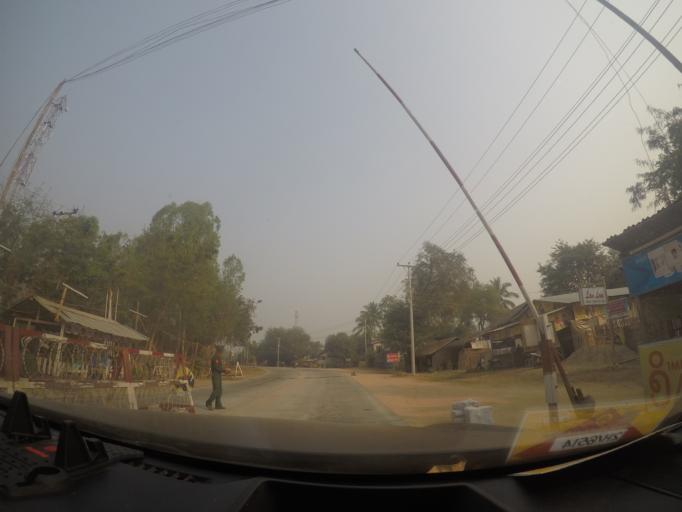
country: MM
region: Mandalay
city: Nay Pyi Taw
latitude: 19.9032
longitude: 96.0256
